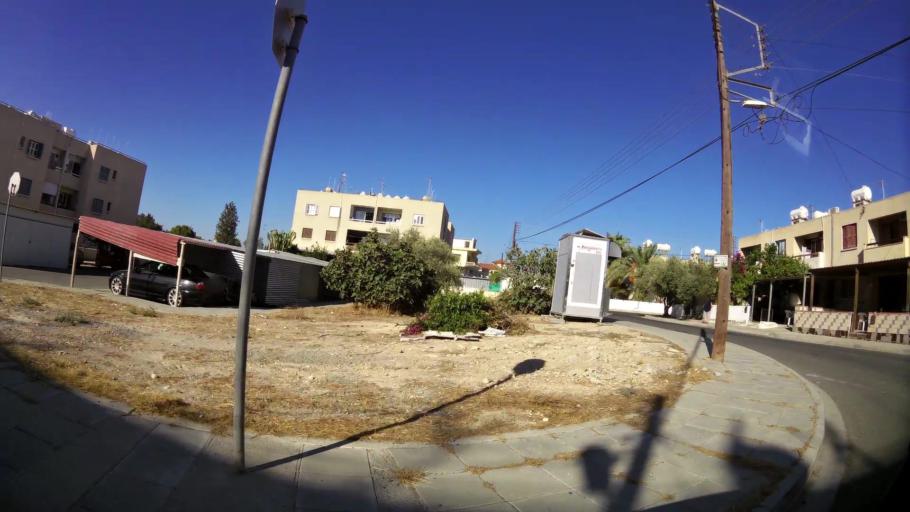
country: CY
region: Larnaka
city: Larnaca
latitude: 34.9272
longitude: 33.6103
